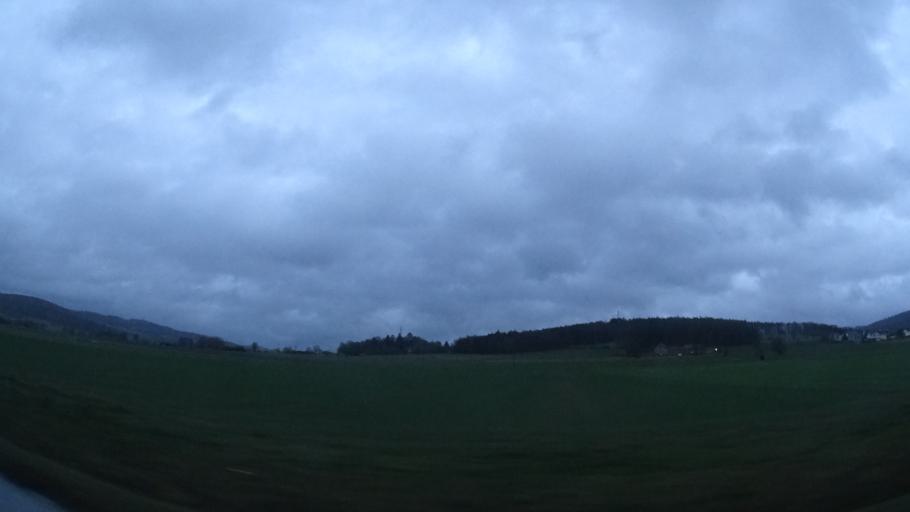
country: DE
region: Bavaria
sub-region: Regierungsbezirk Unterfranken
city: Motten
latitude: 50.4450
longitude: 9.7754
